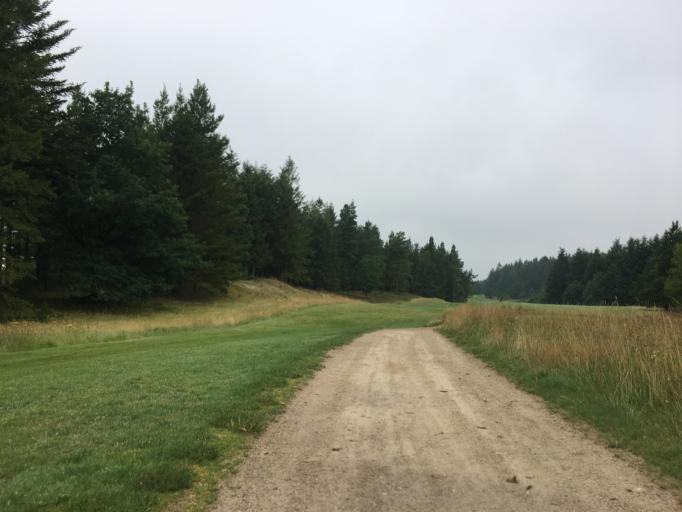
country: DK
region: Central Jutland
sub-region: Holstebro Kommune
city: Ulfborg
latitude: 56.3249
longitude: 8.4322
